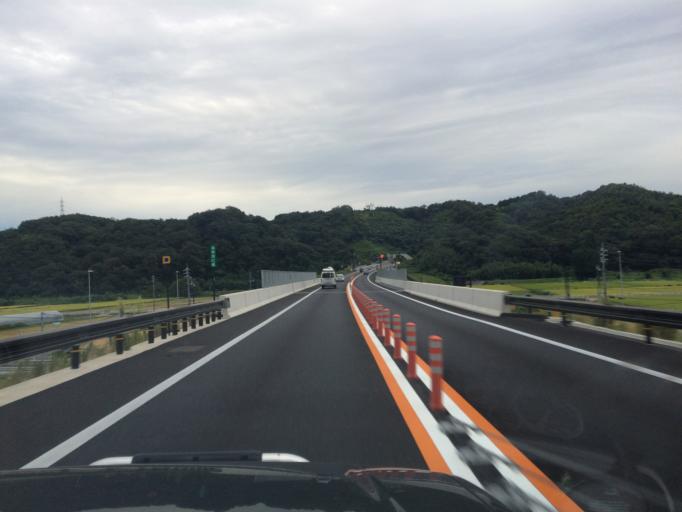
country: JP
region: Tottori
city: Tottori
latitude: 35.4940
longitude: 134.1898
